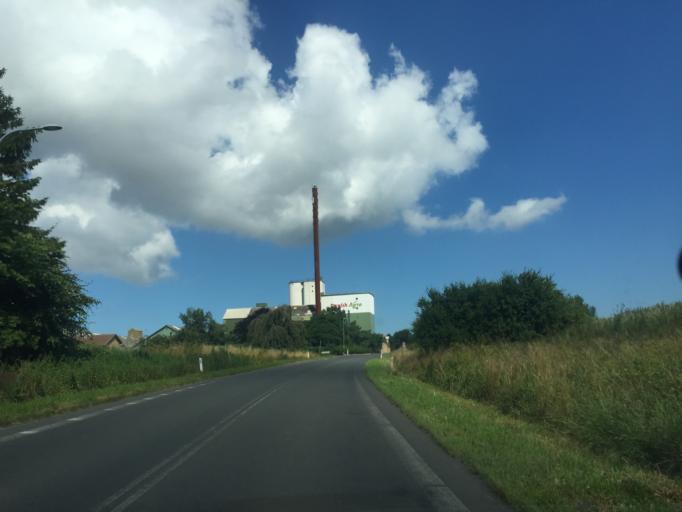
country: DK
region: South Denmark
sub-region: Nordfyns Kommune
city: Otterup
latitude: 55.5337
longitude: 10.3860
